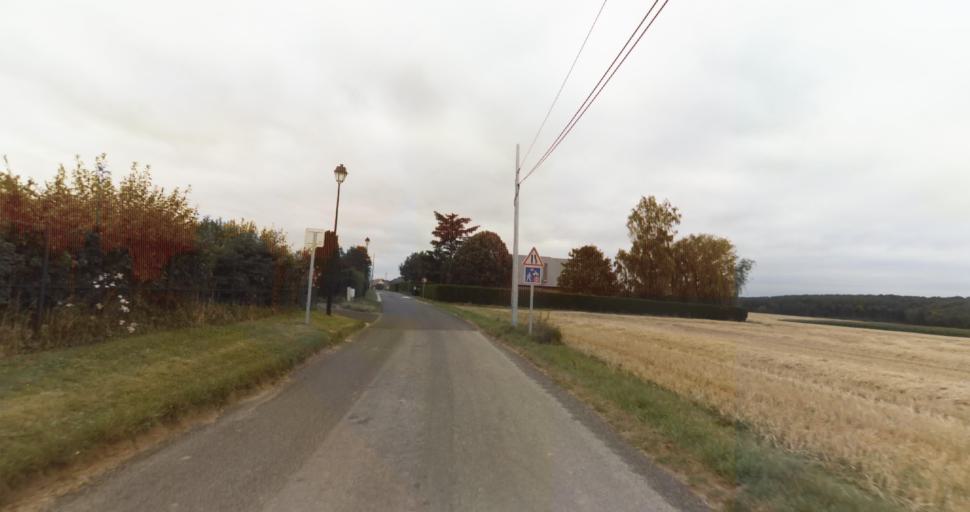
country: FR
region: Haute-Normandie
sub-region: Departement de l'Eure
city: Marcilly-sur-Eure
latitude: 48.8871
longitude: 1.3023
